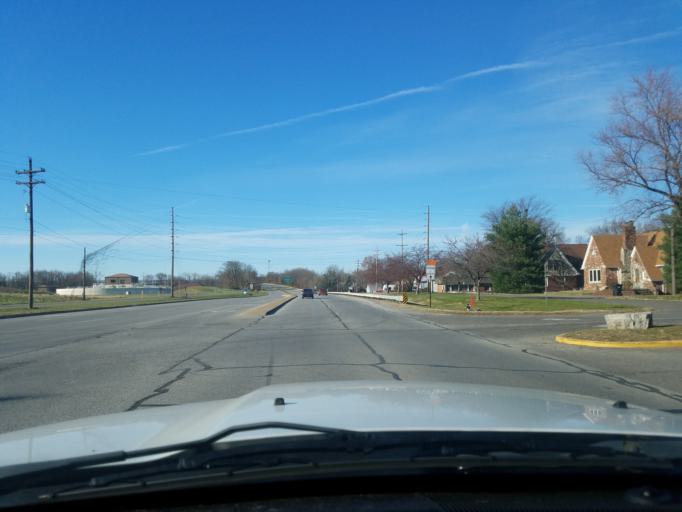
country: US
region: Indiana
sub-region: Clark County
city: Clarksville
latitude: 38.2945
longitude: -85.7702
